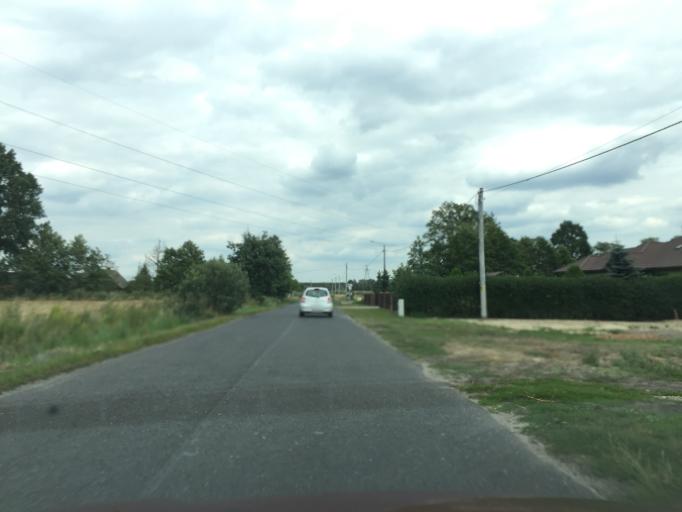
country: PL
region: Greater Poland Voivodeship
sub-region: Powiat kaliski
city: Stawiszyn
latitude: 51.9541
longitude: 18.1706
